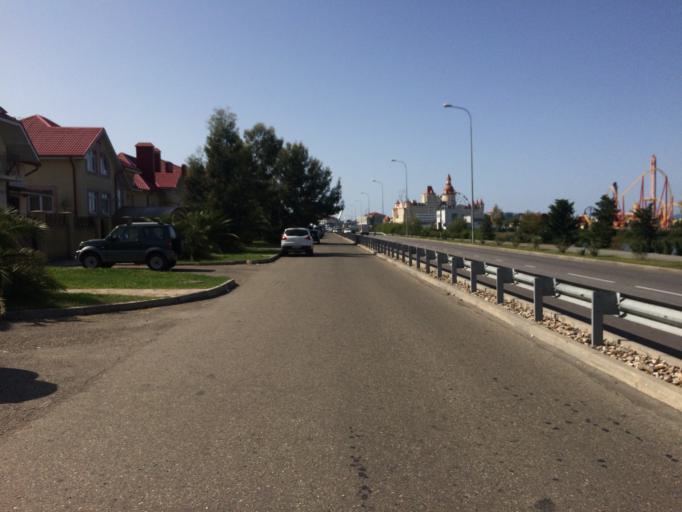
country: RU
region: Krasnodarskiy
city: Adler
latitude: 43.3996
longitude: 39.9716
